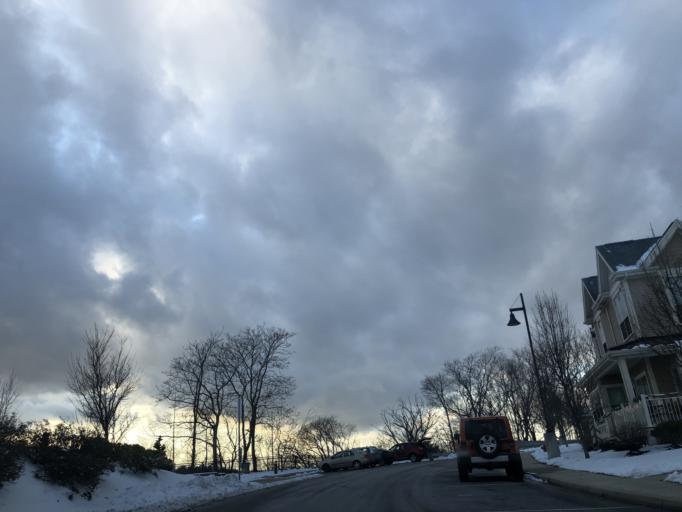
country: US
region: Massachusetts
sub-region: Middlesex County
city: Arlington
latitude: 42.4236
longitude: -71.1616
